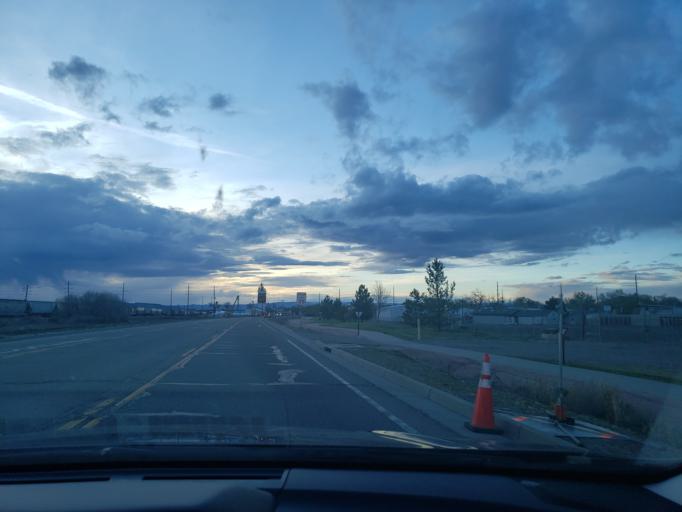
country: US
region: Colorado
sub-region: Mesa County
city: Fruita
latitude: 39.1519
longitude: -108.7262
